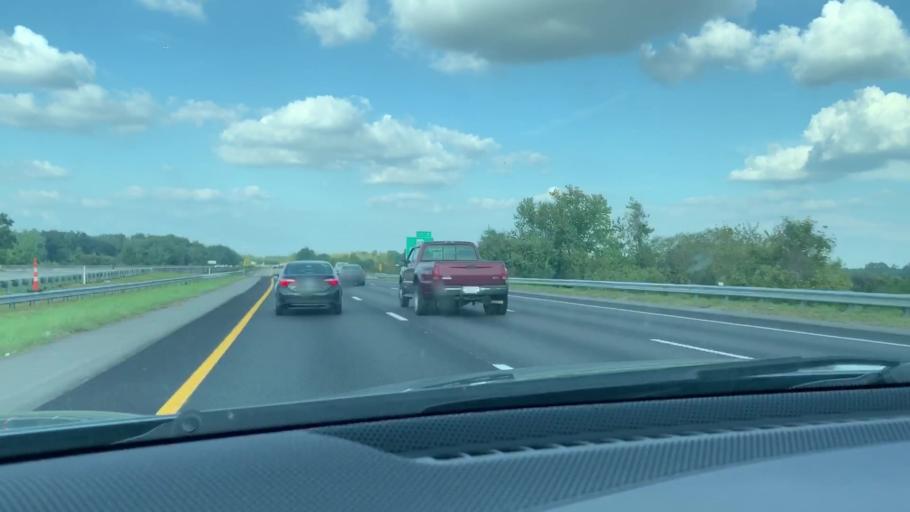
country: US
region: South Carolina
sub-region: Richland County
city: Columbia
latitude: 33.9387
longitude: -81.0061
